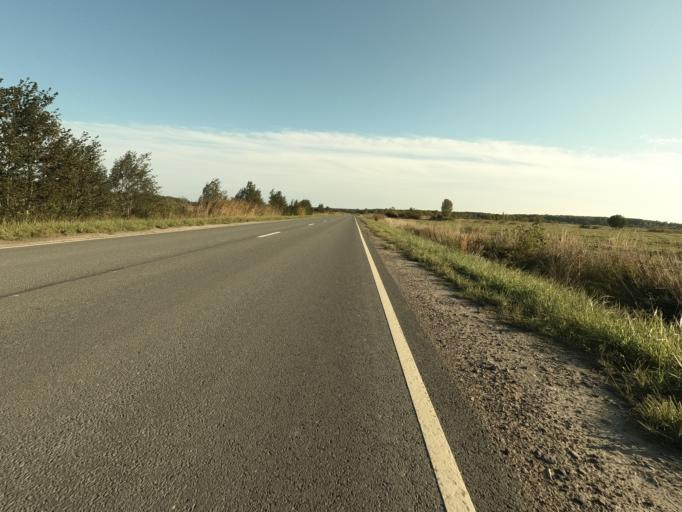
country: RU
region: St.-Petersburg
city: Sapernyy
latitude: 59.7368
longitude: 30.6543
